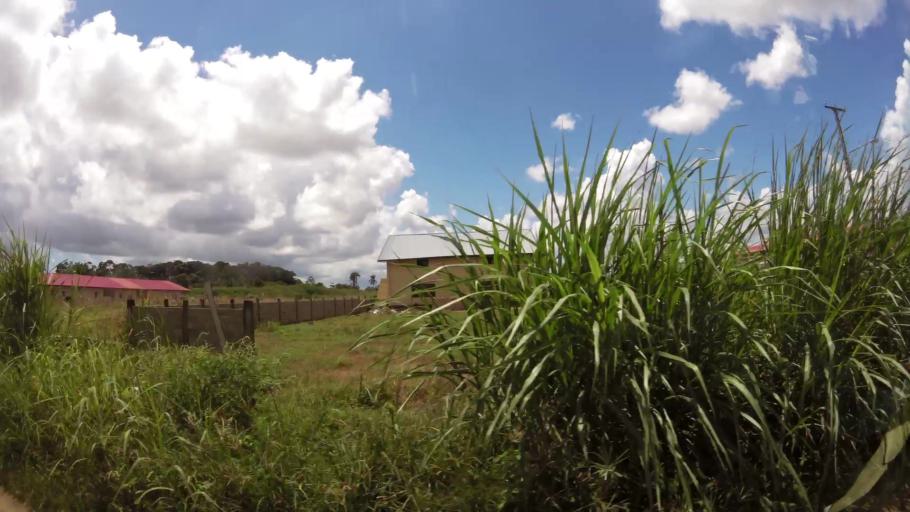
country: SR
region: Paramaribo
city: Paramaribo
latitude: 5.8567
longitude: -55.1664
